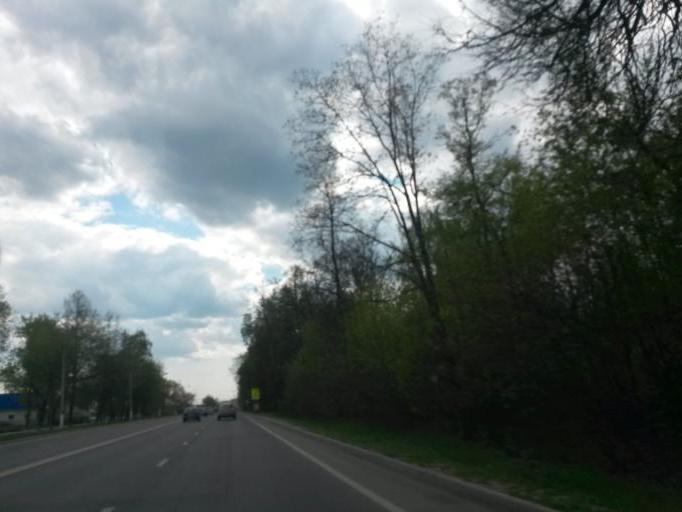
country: RU
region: Moskovskaya
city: Klimovsk
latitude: 55.3711
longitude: 37.5321
